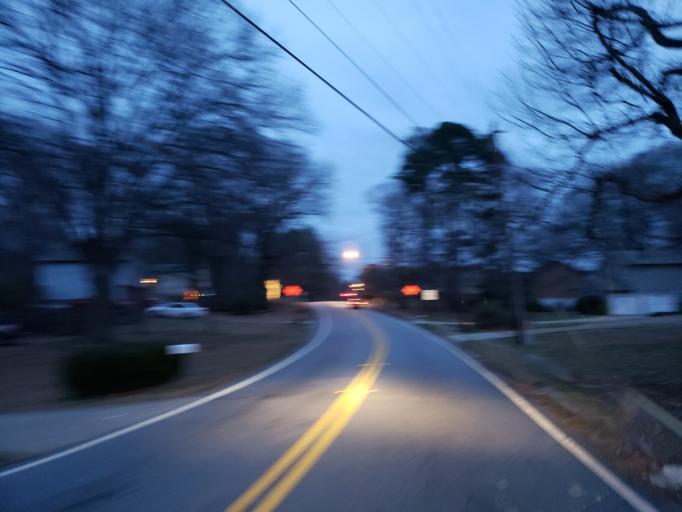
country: US
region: Georgia
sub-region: Cobb County
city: Mableton
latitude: 33.8446
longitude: -84.5824
